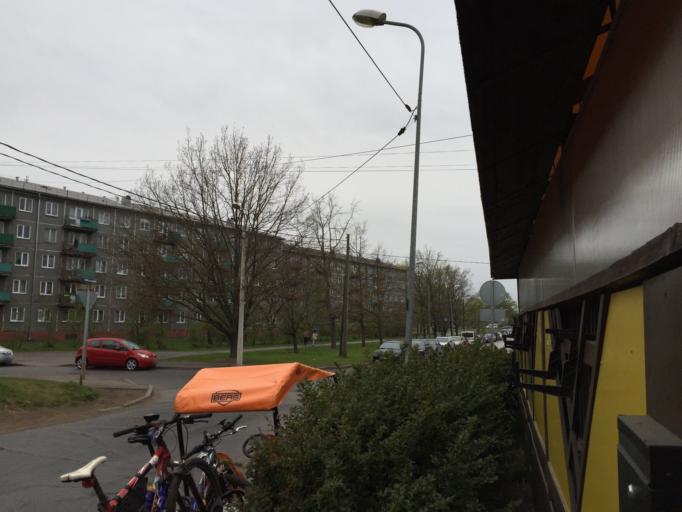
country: LV
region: Riga
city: Jaunciems
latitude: 57.0199
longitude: 24.1375
